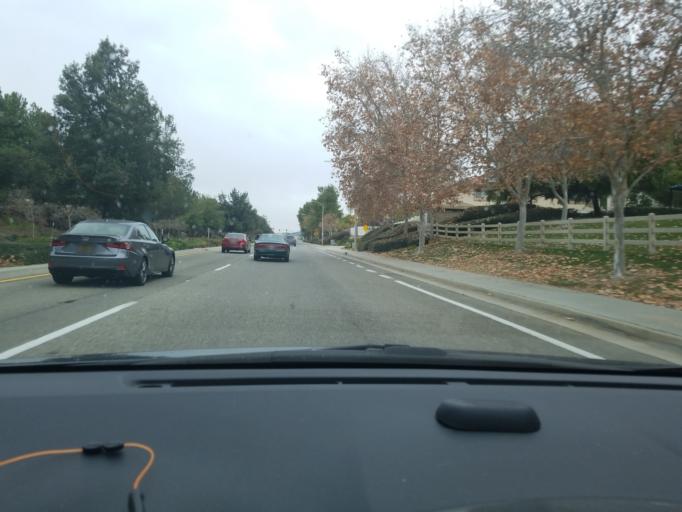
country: US
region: California
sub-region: Riverside County
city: Murrieta Hot Springs
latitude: 33.5432
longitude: -117.1523
